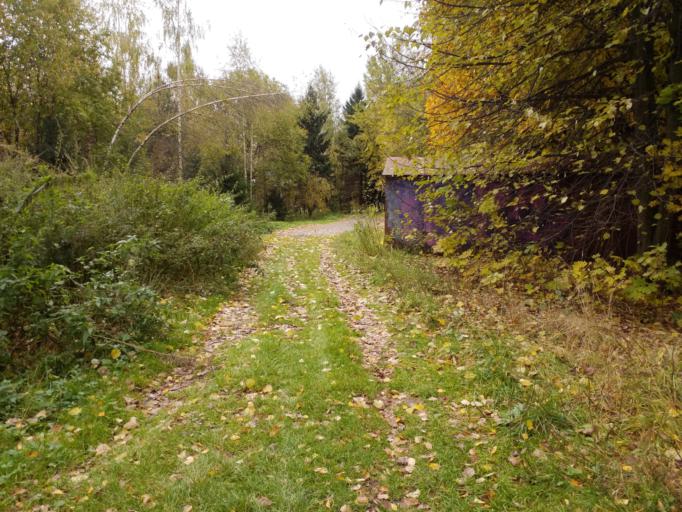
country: RU
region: Moskovskaya
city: Ashukino
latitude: 56.1606
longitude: 37.9598
